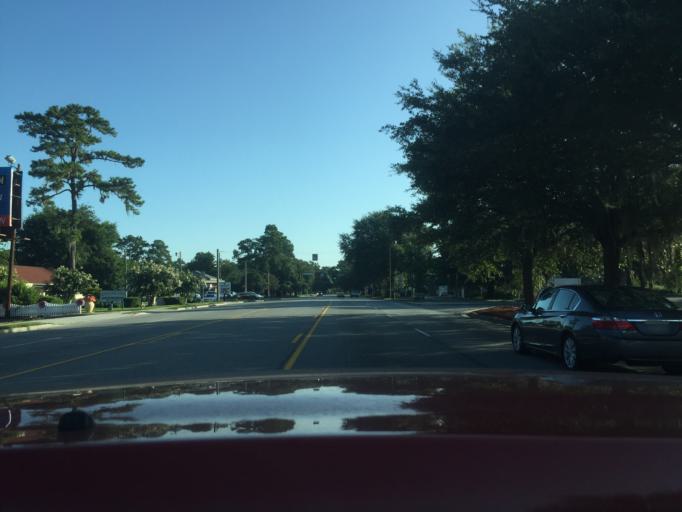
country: US
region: Georgia
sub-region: Chatham County
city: Isle of Hope
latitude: 32.0086
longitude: -81.1002
